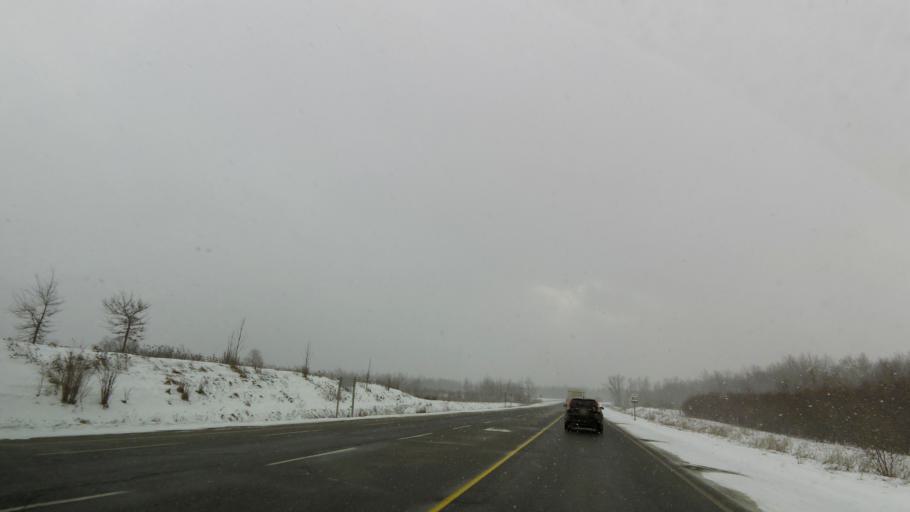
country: CA
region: Ontario
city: Orangeville
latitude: 43.8986
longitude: -80.0980
